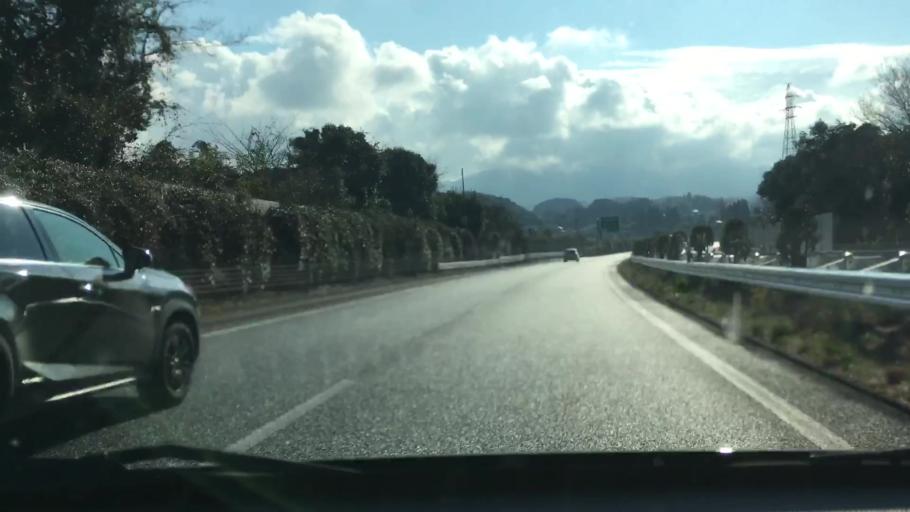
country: JP
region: Kumamoto
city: Matsubase
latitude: 32.5838
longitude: 130.7160
